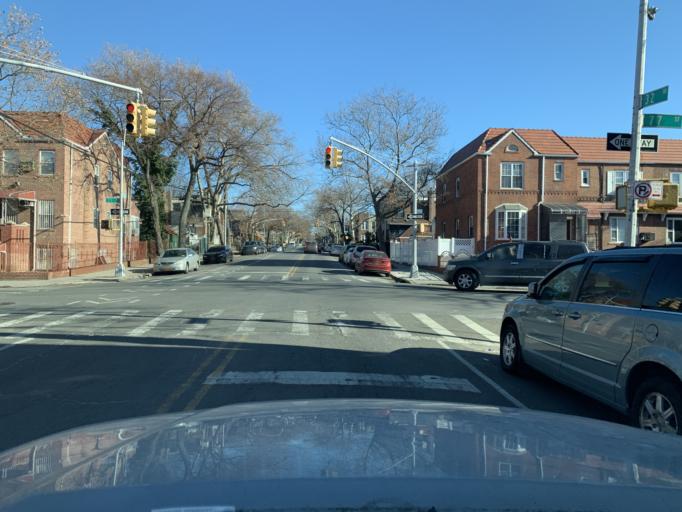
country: US
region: New York
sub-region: Queens County
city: Long Island City
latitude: 40.7571
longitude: -73.8906
